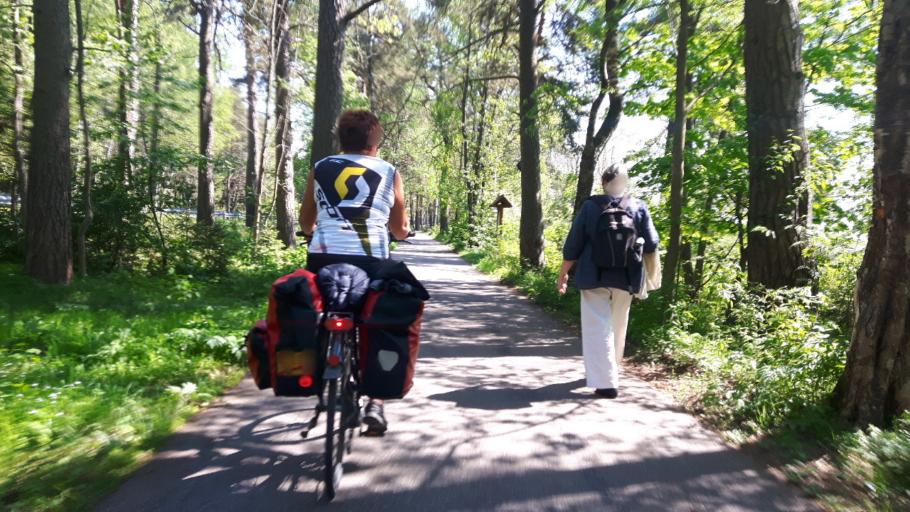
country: RU
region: St.-Petersburg
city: Komarovo
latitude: 60.1773
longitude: 29.7902
